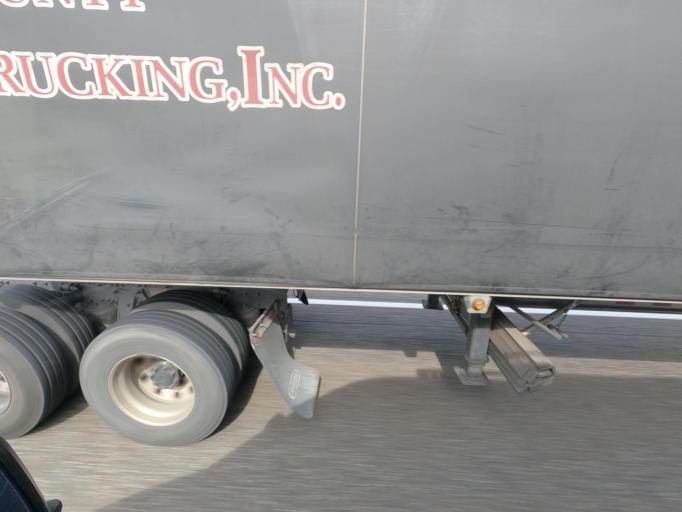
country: US
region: Tennessee
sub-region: Henderson County
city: Lexington
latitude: 35.8029
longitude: -88.3307
